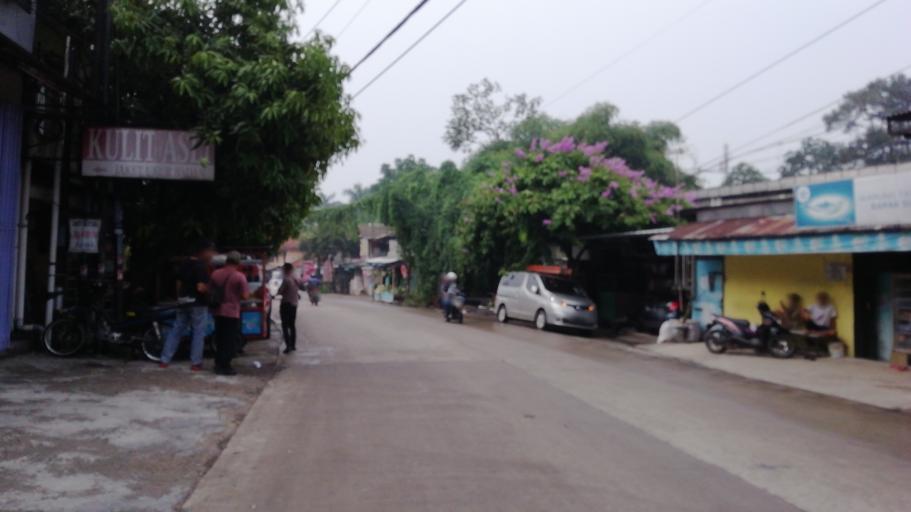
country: ID
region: West Java
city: Bogor
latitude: -6.5586
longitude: 106.8128
